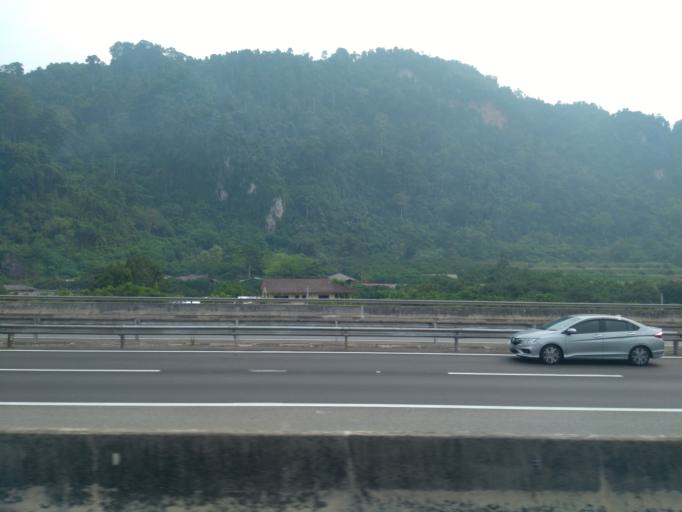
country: MY
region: Perak
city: Ipoh
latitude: 4.6027
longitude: 101.1397
